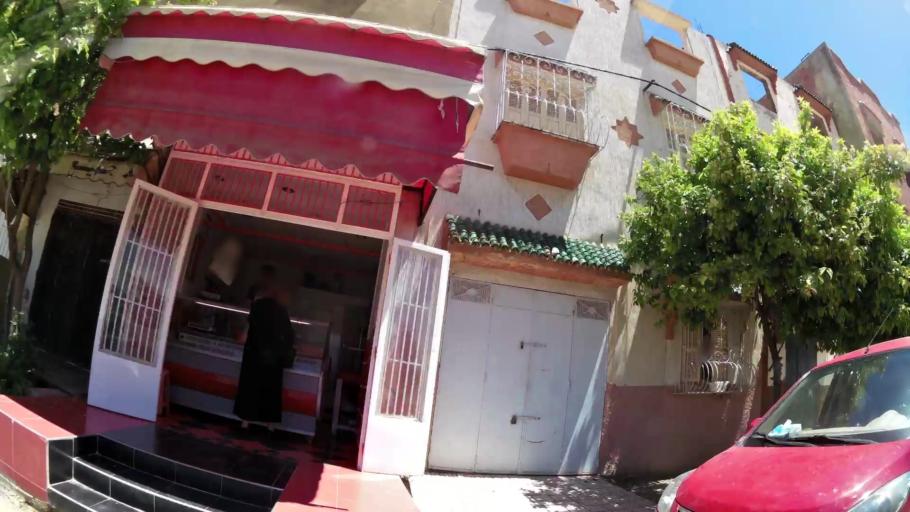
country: MA
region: Meknes-Tafilalet
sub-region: Meknes
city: Meknes
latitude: 33.9067
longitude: -5.5589
